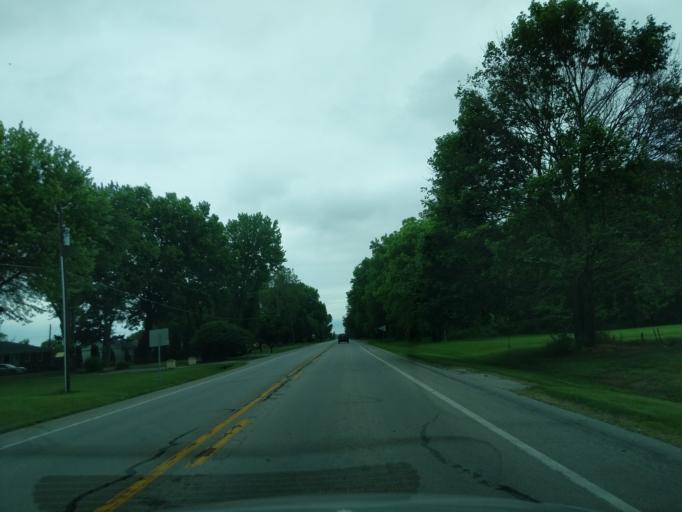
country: US
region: Indiana
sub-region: Hamilton County
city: Noblesville
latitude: 40.0737
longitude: -86.0146
